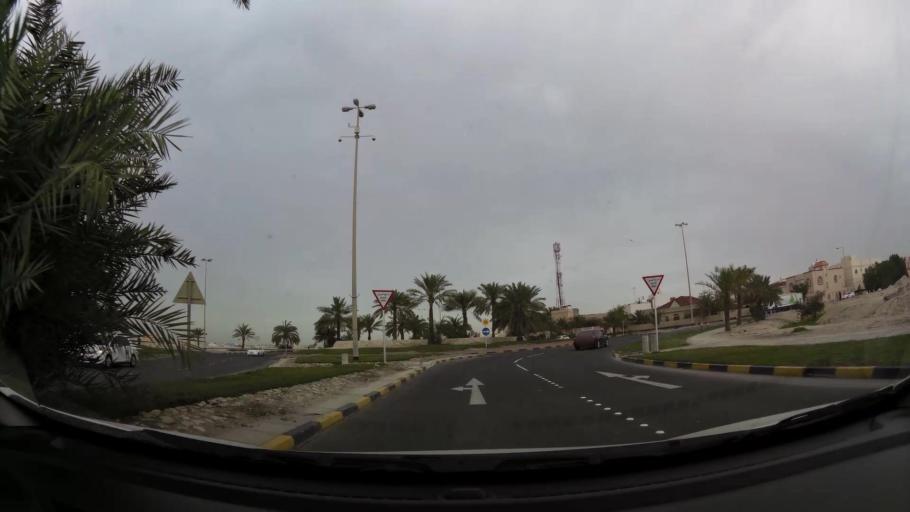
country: BH
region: Central Governorate
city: Dar Kulayb
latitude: 26.0713
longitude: 50.5077
